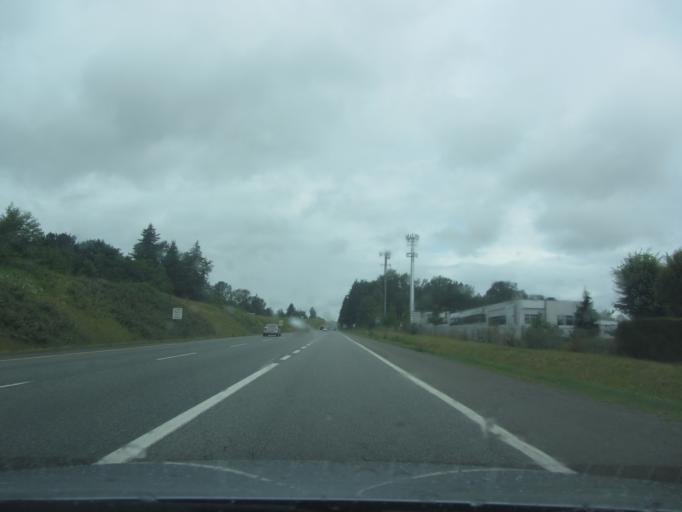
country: CA
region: British Columbia
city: Aldergrove
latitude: 49.0608
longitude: -122.3887
